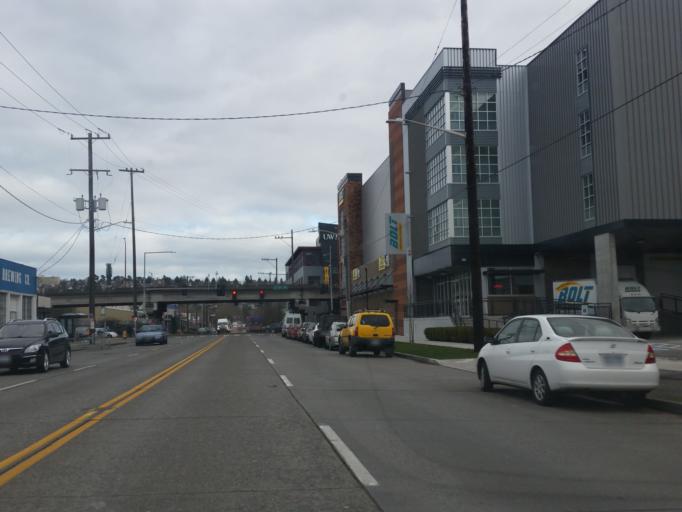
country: US
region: Washington
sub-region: King County
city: Seattle
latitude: 47.6637
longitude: -122.3778
